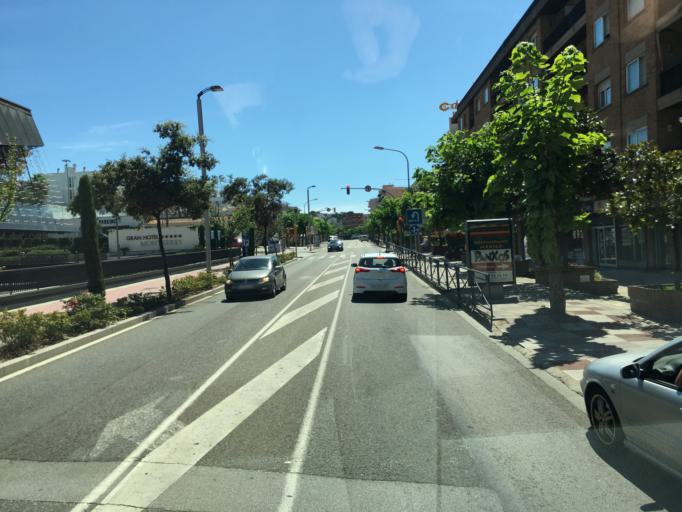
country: ES
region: Catalonia
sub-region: Provincia de Girona
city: Lloret de Mar
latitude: 41.7041
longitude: 2.8501
